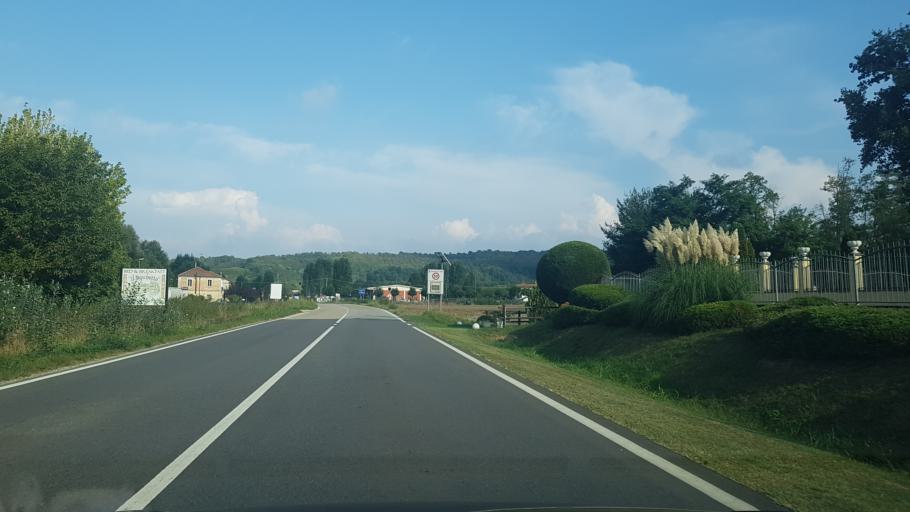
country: IT
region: Piedmont
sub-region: Provincia di Asti
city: Bruno
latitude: 44.7976
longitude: 8.4366
